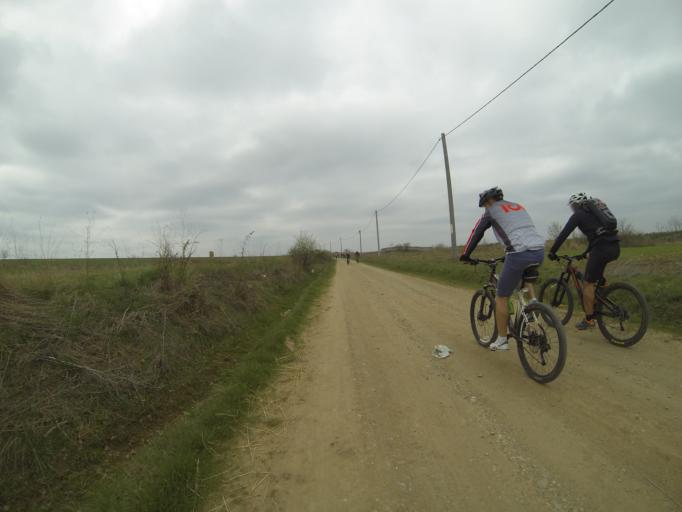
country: RO
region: Dolj
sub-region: Comuna Breasta
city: Breasta
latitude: 44.3410
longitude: 23.6728
